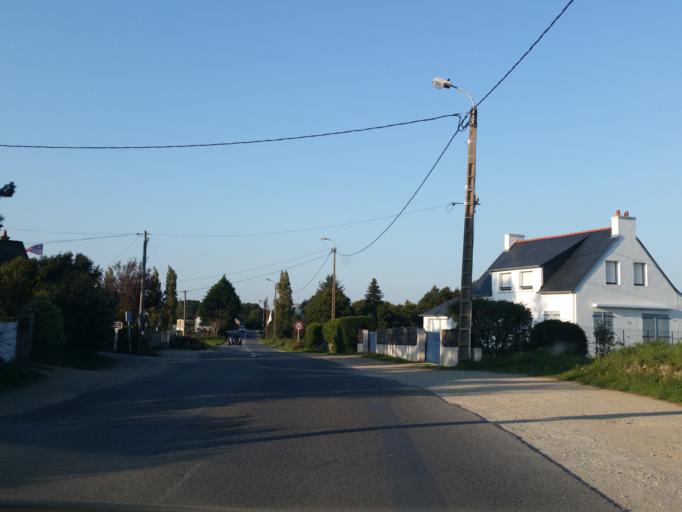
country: FR
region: Brittany
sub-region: Departement du Morbihan
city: Carnac
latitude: 47.5907
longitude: -3.0762
